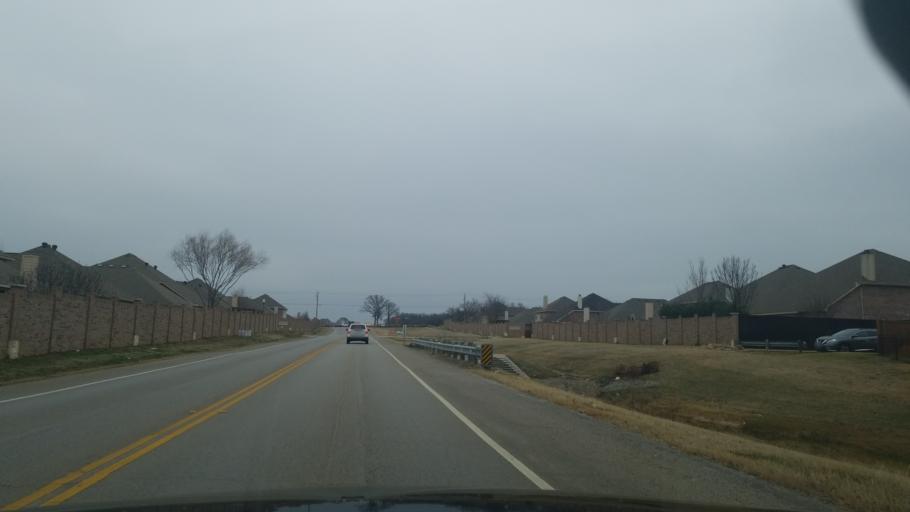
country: US
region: Texas
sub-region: Denton County
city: Corinth
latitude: 33.1683
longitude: -97.0711
